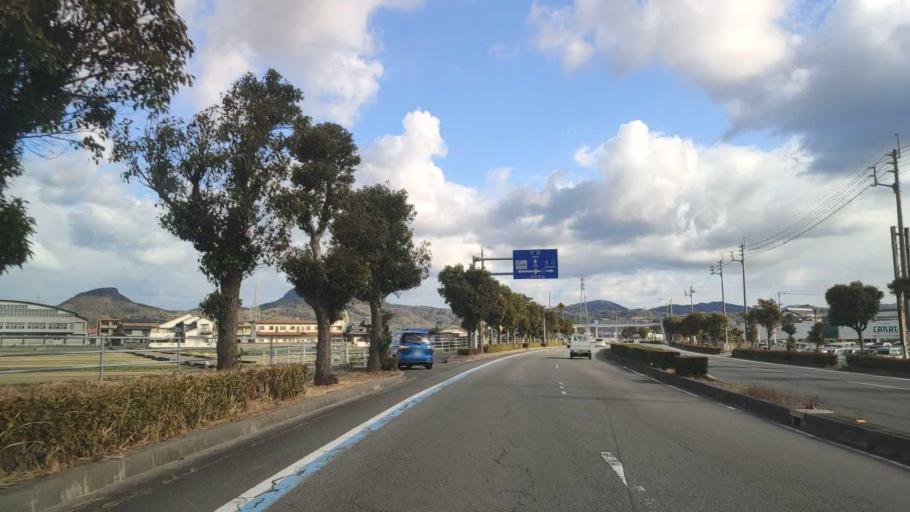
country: JP
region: Ehime
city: Hojo
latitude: 33.9677
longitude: 132.7802
